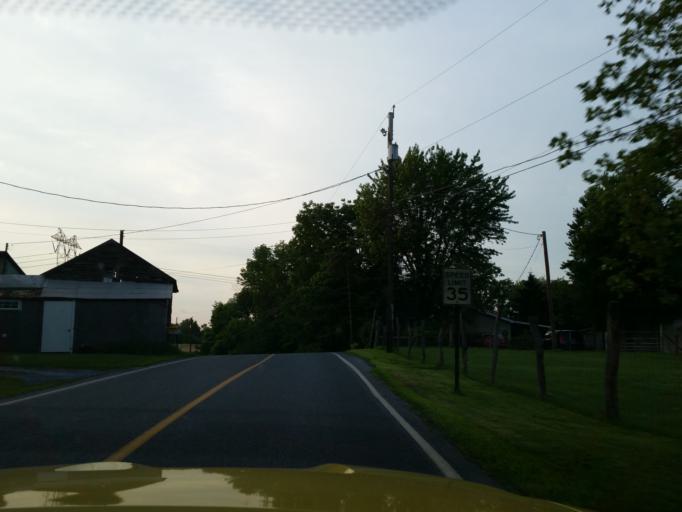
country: US
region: Pennsylvania
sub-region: Lebanon County
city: Jonestown
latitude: 40.4123
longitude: -76.5144
